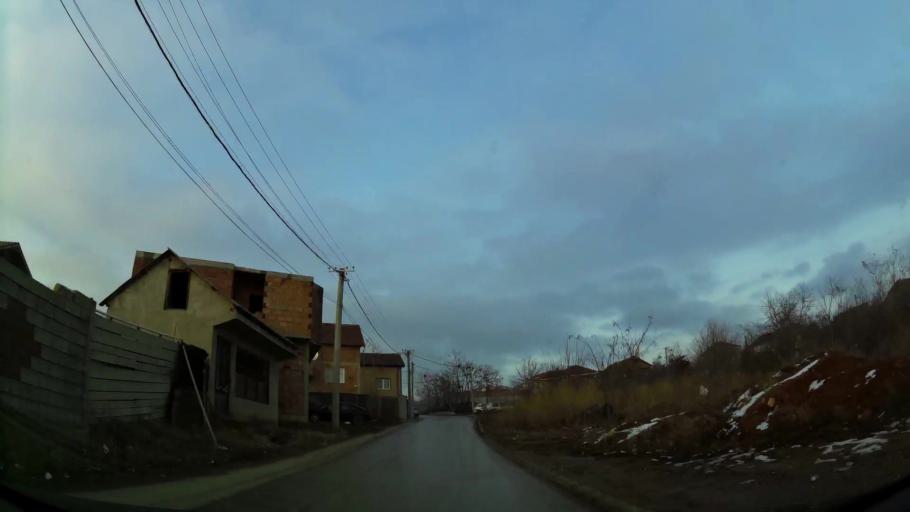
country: MK
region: Aracinovo
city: Arachinovo
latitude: 42.0255
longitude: 21.5729
